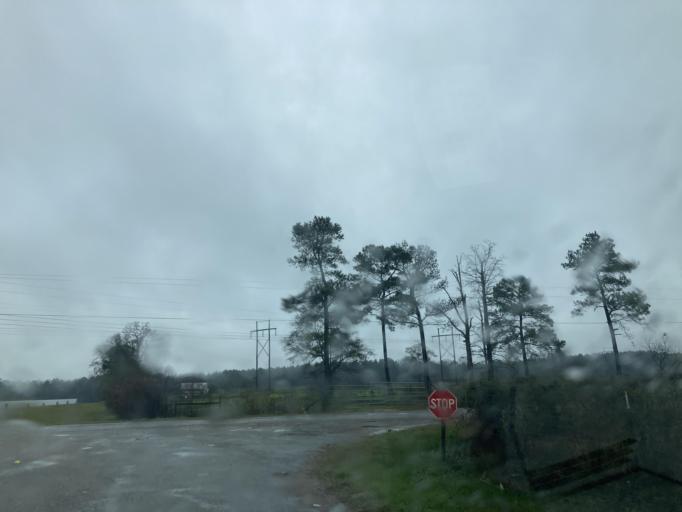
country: US
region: Mississippi
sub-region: Forrest County
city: Rawls Springs
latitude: 31.4813
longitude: -89.3907
